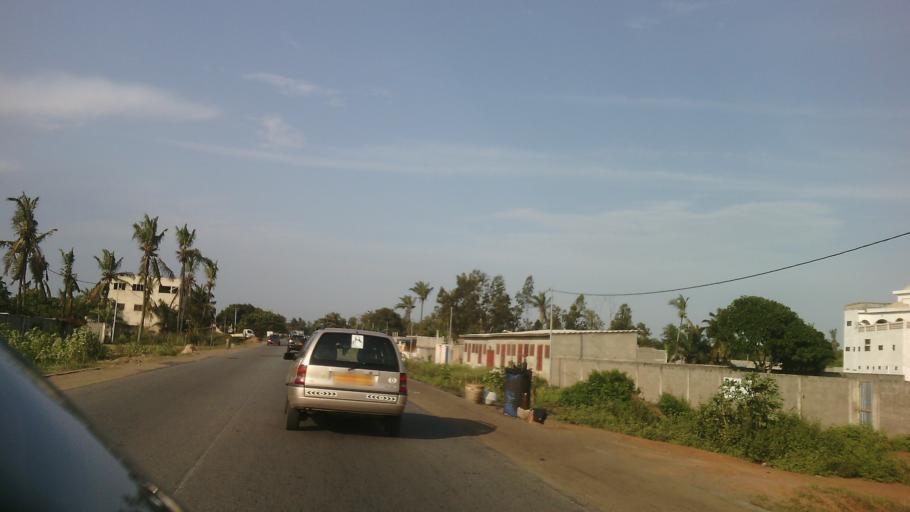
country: TG
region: Maritime
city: Vogan
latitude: 6.2011
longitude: 1.4069
